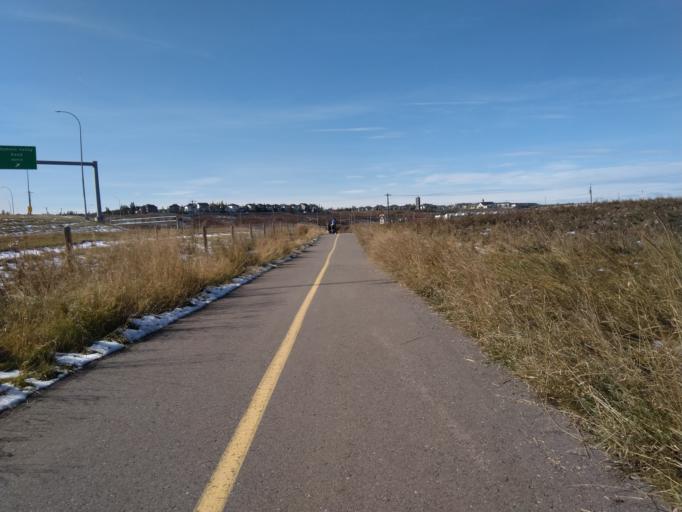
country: CA
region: Alberta
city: Calgary
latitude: 51.1588
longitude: -114.1158
